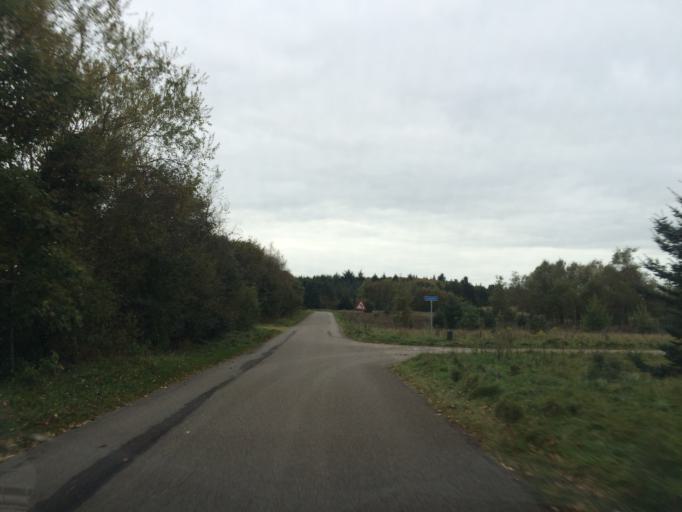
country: DK
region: Central Jutland
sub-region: Holstebro Kommune
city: Ulfborg
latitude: 56.2261
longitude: 8.4347
